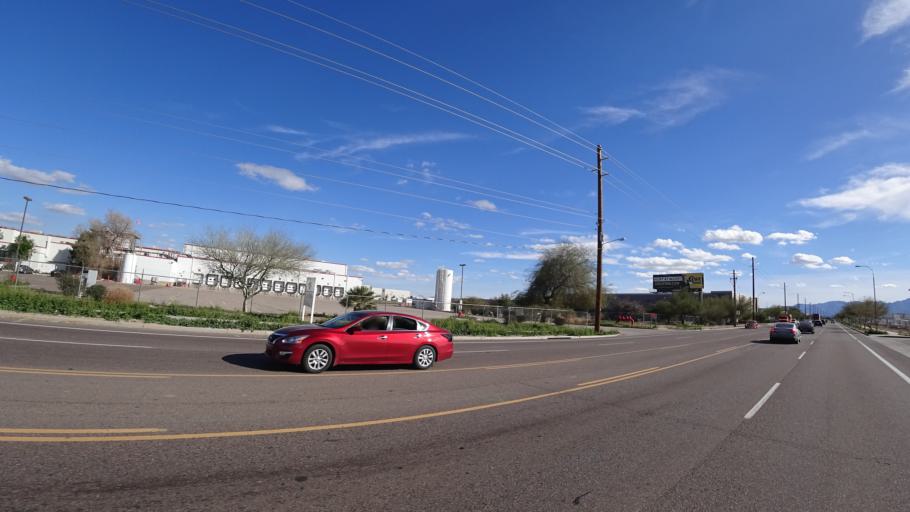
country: US
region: Arizona
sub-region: Maricopa County
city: Tolleson
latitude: 33.4431
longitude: -112.2212
